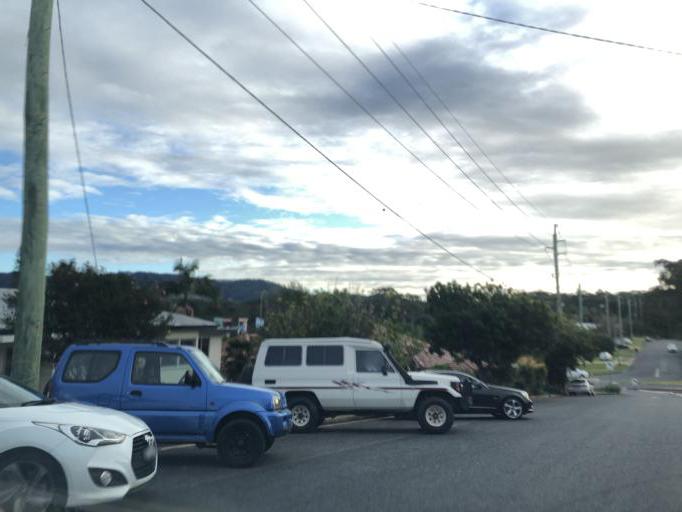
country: AU
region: New South Wales
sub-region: Coffs Harbour
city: Coffs Harbour
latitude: -30.3042
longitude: 153.1238
